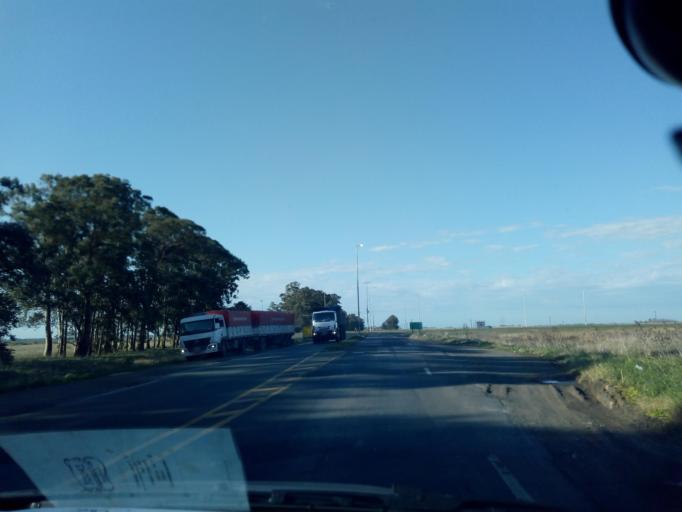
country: AR
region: Buenos Aires
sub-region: Partido de Ayacucho
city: Ayacucho
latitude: -37.2275
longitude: -58.4980
